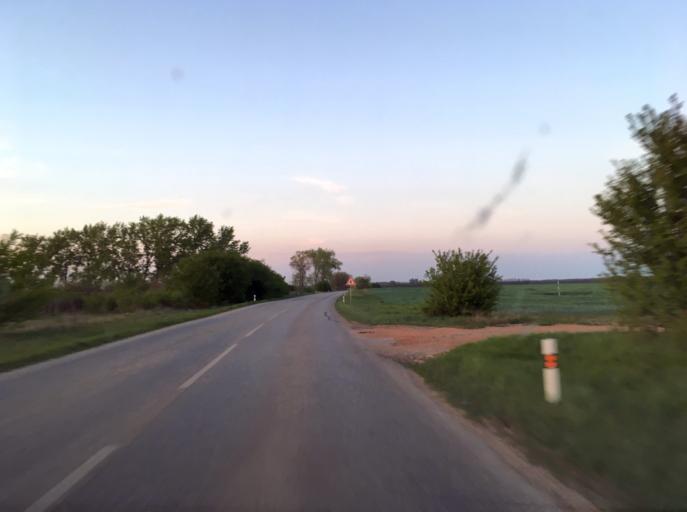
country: SK
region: Nitriansky
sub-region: Okres Nove Zamky
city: Nove Zamky
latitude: 47.9408
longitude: 18.1290
